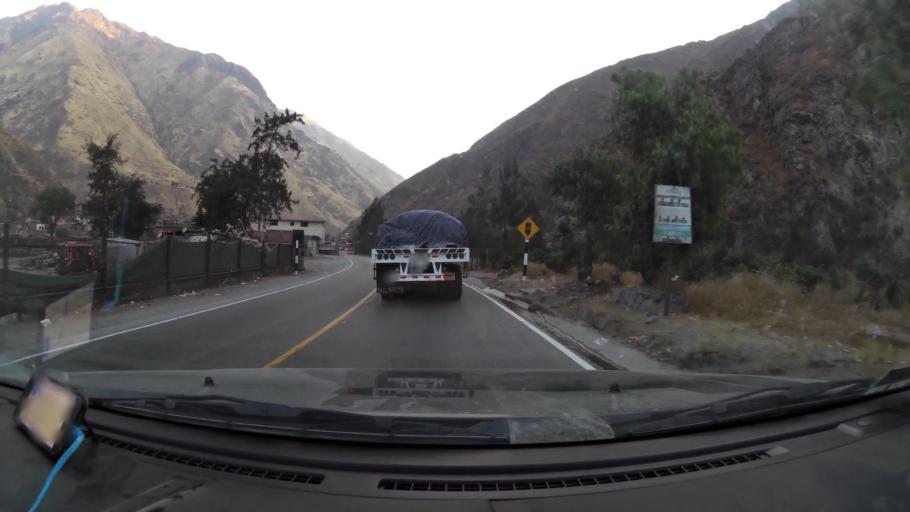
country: PE
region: Lima
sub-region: Provincia de Huarochiri
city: Matucana
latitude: -11.8441
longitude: -76.3870
